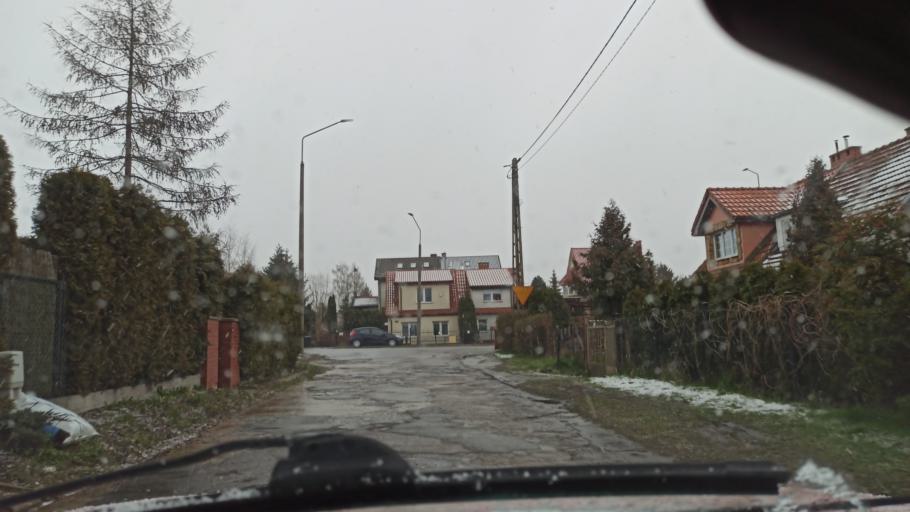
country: PL
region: Warmian-Masurian Voivodeship
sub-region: Powiat elblaski
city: Elblag
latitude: 54.1811
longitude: 19.4134
